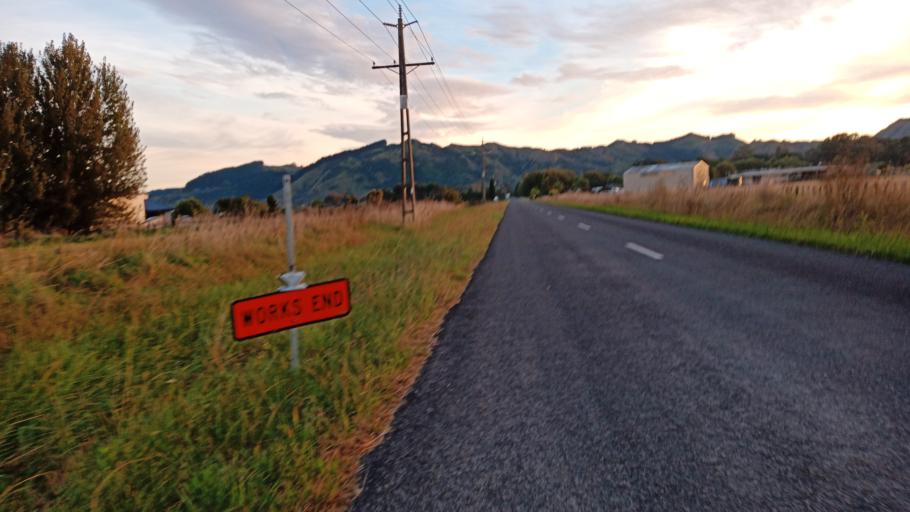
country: NZ
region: Gisborne
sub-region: Gisborne District
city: Gisborne
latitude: -38.6273
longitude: 177.9767
